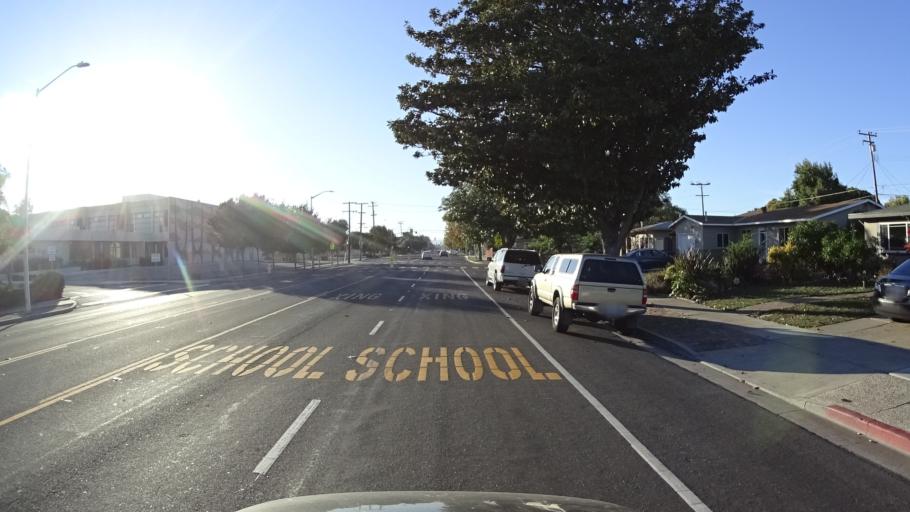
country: US
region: California
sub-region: Santa Clara County
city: Santa Clara
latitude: 37.3669
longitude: -121.9857
